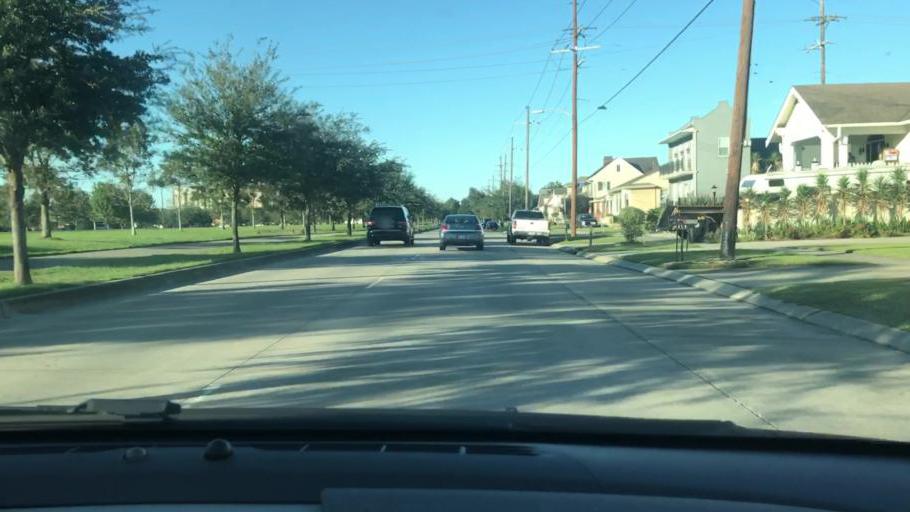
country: US
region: Louisiana
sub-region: Jefferson Parish
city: Metairie
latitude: 30.0099
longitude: -90.1143
